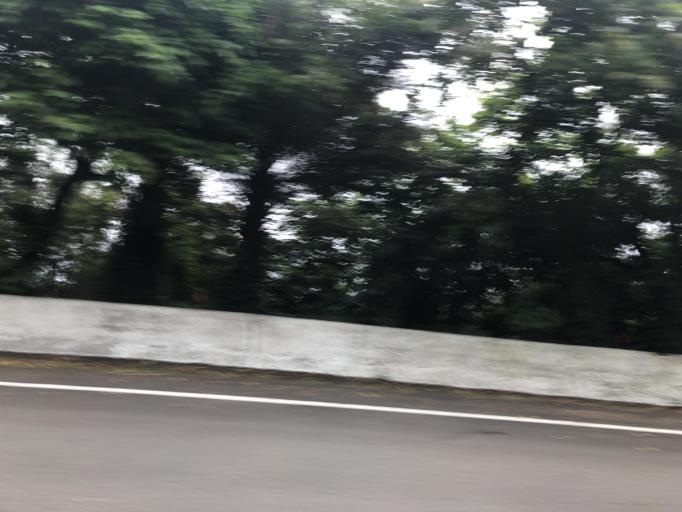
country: TW
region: Taiwan
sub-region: Keelung
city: Keelung
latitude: 25.1984
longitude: 121.6827
